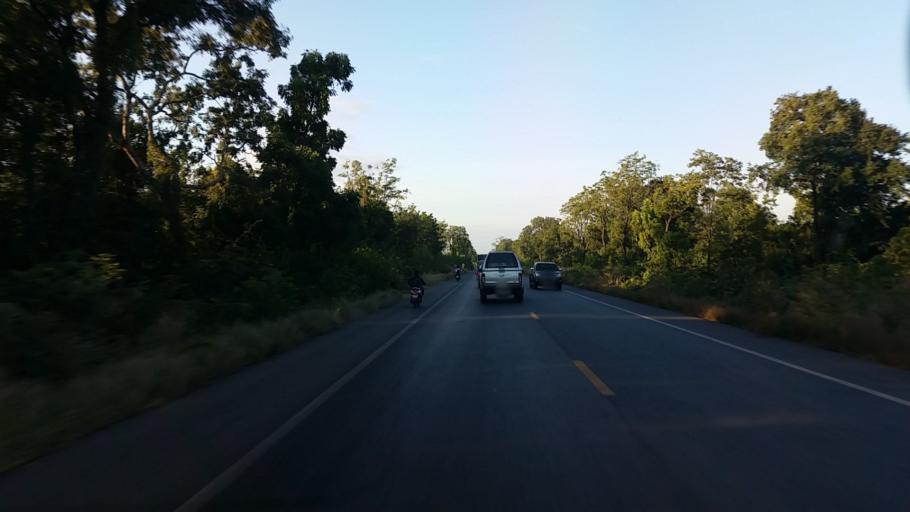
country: TH
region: Lop Buri
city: Chai Badan
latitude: 15.2421
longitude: 101.1662
